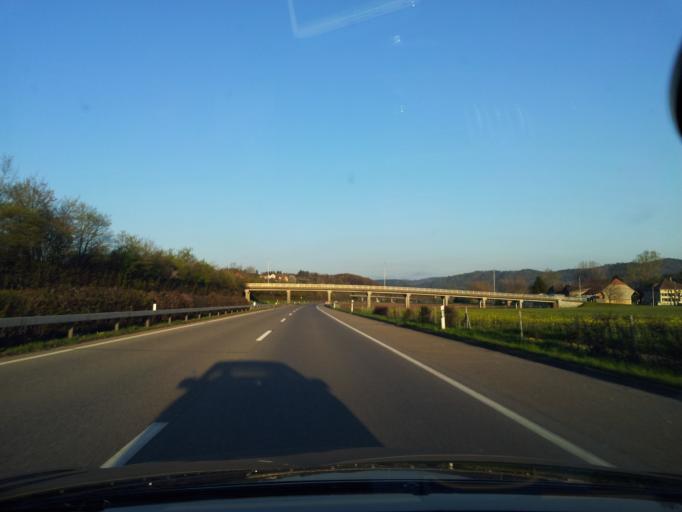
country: CH
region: Bern
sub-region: Bern-Mittelland District
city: Munchenbuchsee
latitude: 47.0314
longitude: 7.4573
